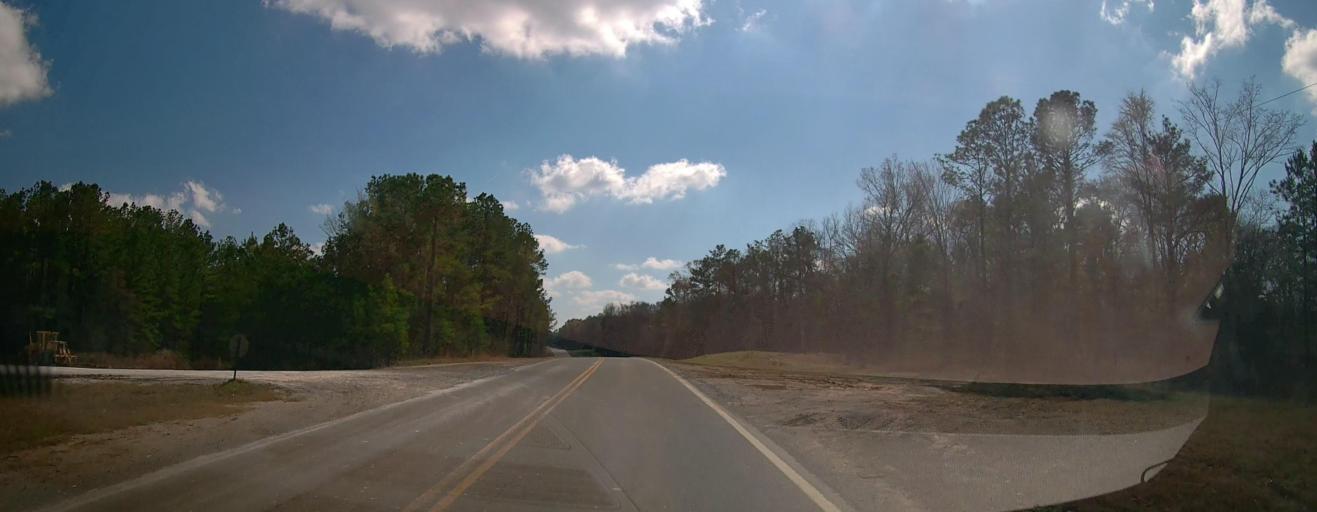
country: US
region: Georgia
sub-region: Wilkinson County
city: Gordon
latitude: 32.7970
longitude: -83.3306
